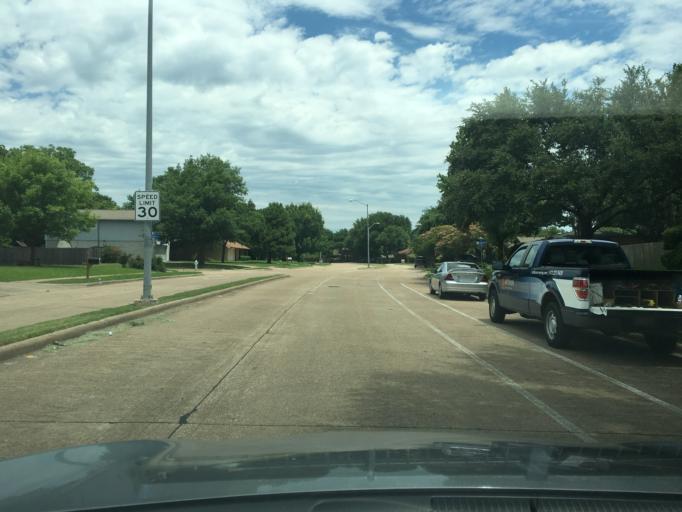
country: US
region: Texas
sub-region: Dallas County
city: Richardson
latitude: 32.9627
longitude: -96.6916
